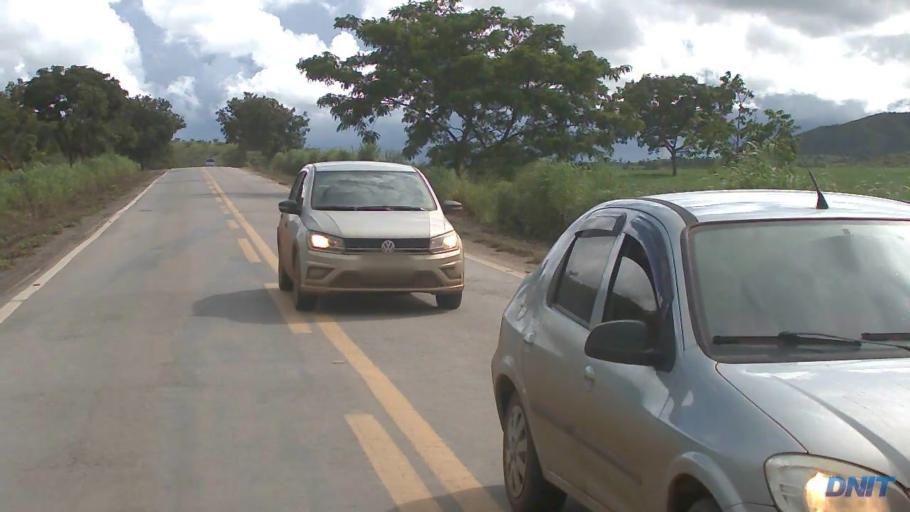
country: BR
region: Goias
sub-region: Padre Bernardo
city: Padre Bernardo
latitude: -15.4540
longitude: -48.2118
